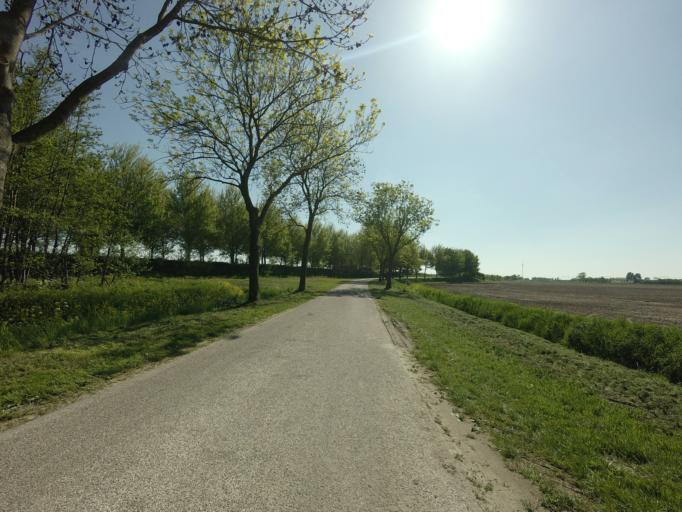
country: NL
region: North Brabant
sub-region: Gemeente Moerdijk
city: Klundert
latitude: 51.6303
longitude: 4.6050
